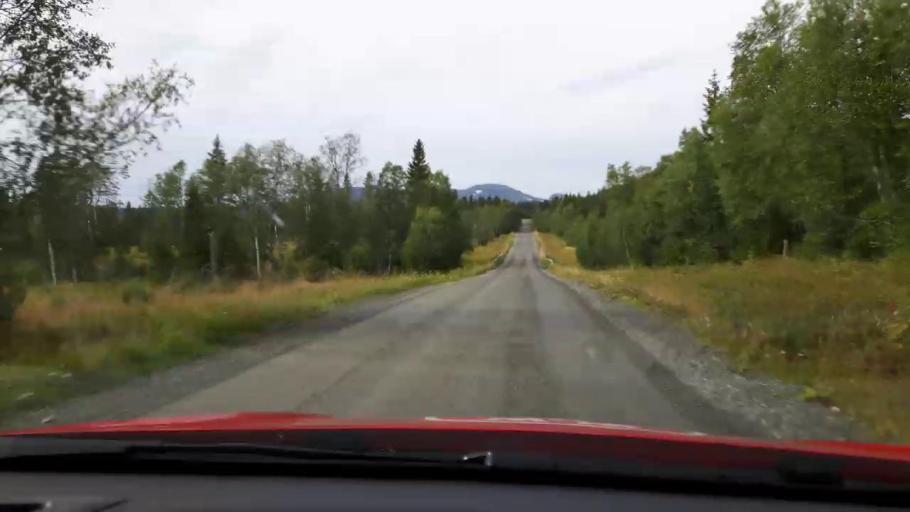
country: SE
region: Jaemtland
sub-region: Are Kommun
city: Are
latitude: 63.7425
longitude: 12.9951
